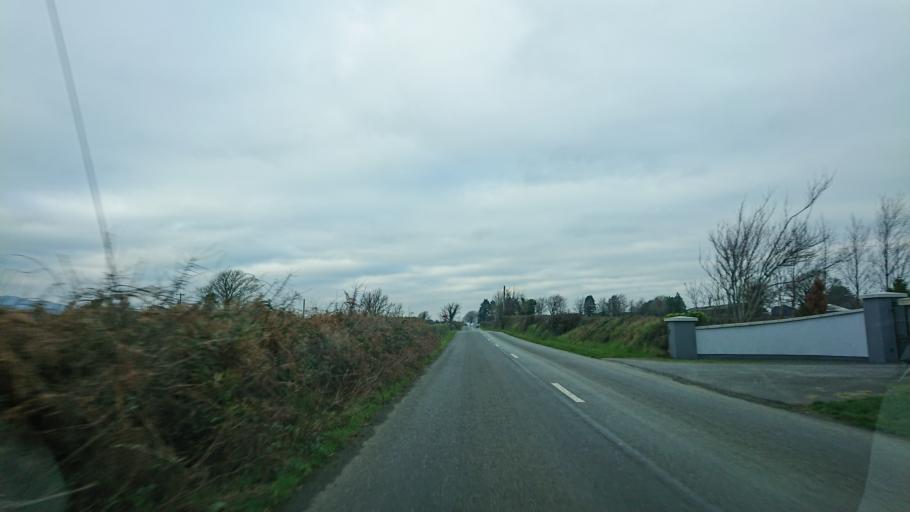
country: IE
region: Munster
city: Carrick-on-Suir
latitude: 52.2927
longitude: -7.4668
